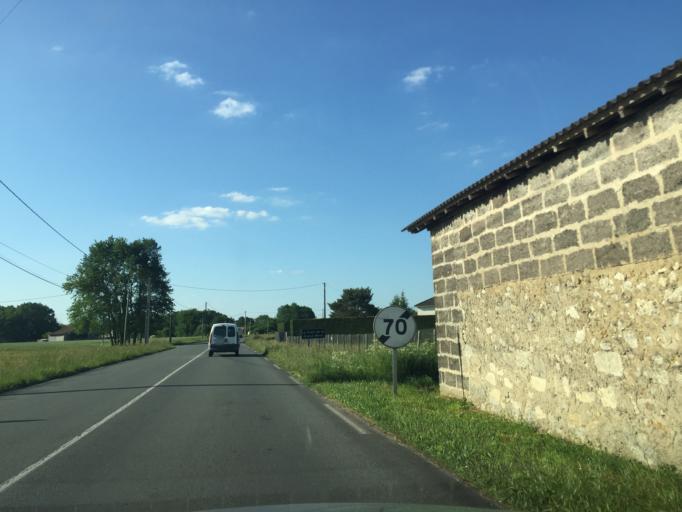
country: FR
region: Poitou-Charentes
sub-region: Departement de la Charente-Maritime
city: Saint-Aigulin
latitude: 45.1236
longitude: -0.0083
